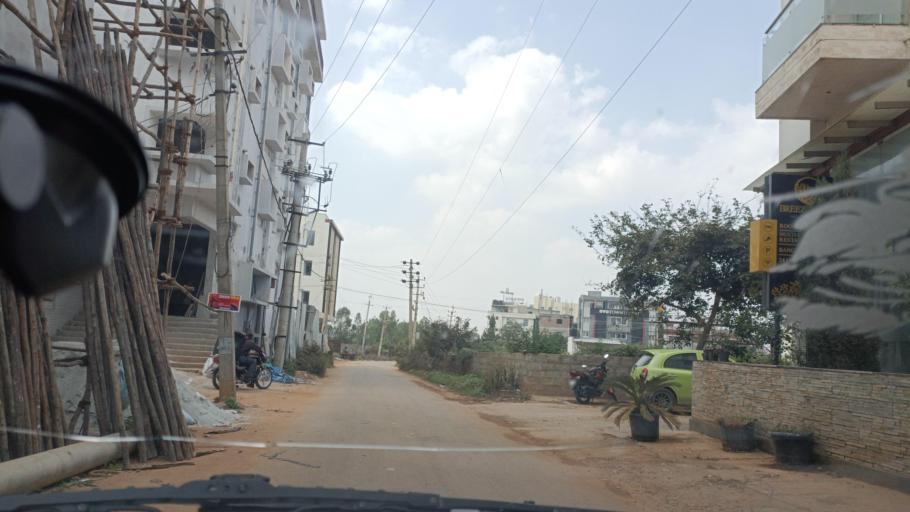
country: IN
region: Karnataka
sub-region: Bangalore Urban
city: Yelahanka
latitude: 13.1631
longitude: 77.6332
